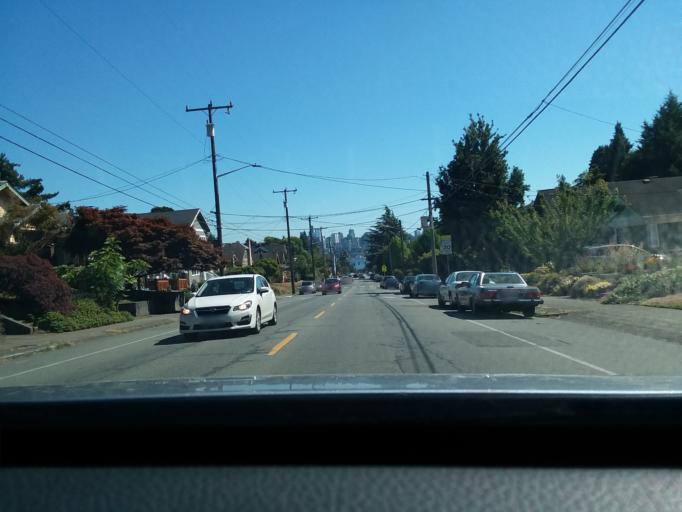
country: US
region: Washington
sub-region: King County
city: Seattle
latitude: 47.6578
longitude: -122.3363
